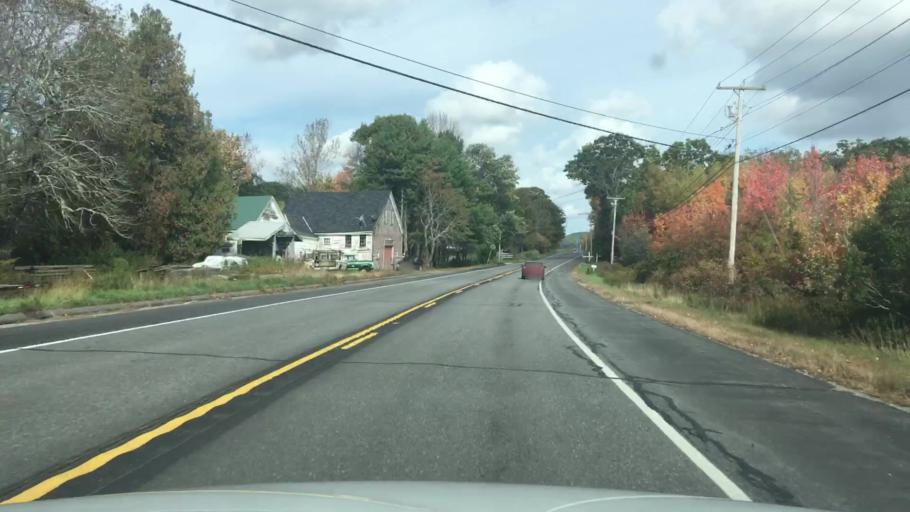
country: US
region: Maine
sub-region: Knox County
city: Rockport
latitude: 44.1611
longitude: -69.1176
